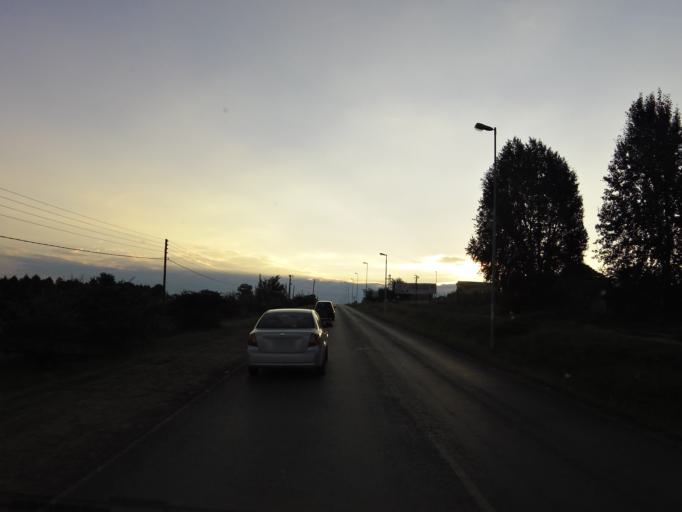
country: LS
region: Leribe
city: Leribe
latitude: -28.8681
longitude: 28.0622
